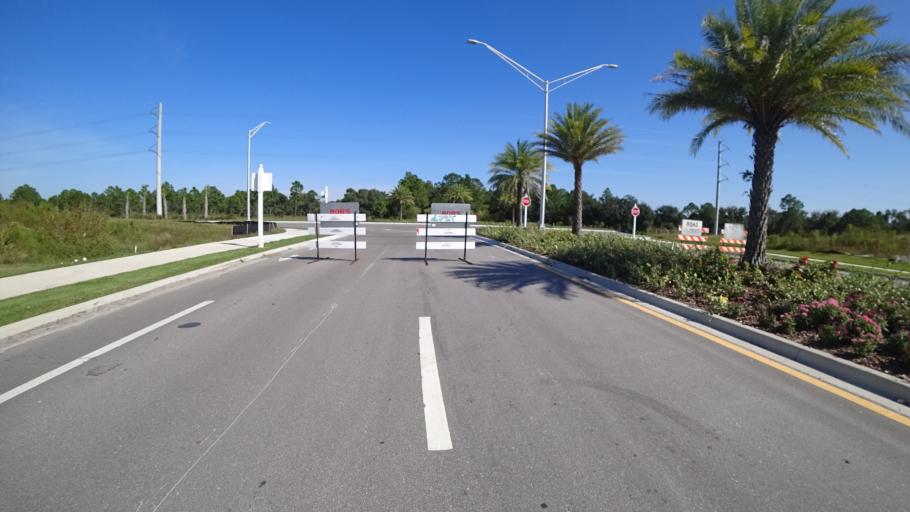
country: US
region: Florida
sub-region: Sarasota County
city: The Meadows
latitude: 27.4027
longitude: -82.3548
